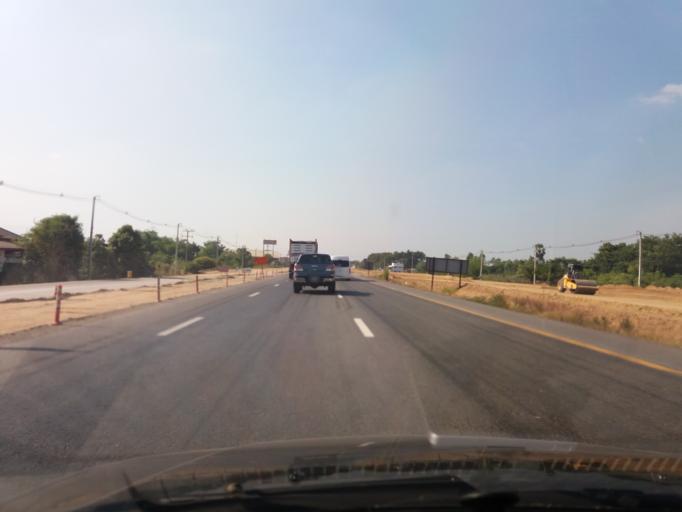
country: TH
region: Nakhon Sawan
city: Nakhon Sawan
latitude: 15.6367
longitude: 100.0971
